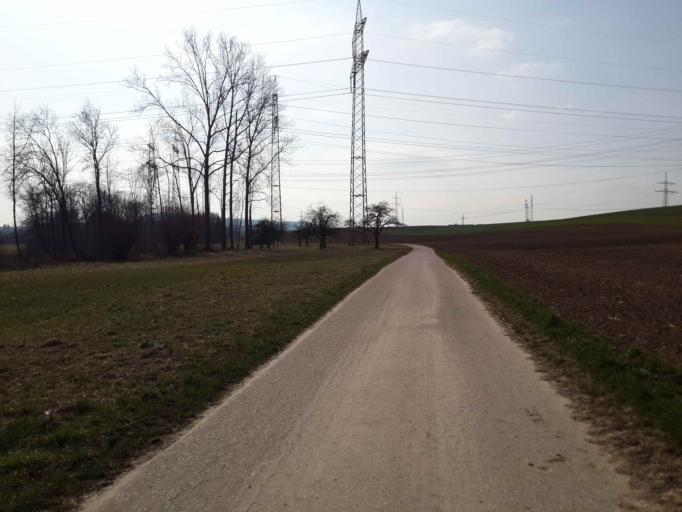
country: DE
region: Baden-Wuerttemberg
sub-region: Regierungsbezirk Stuttgart
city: Leingarten
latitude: 49.1488
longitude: 9.1497
